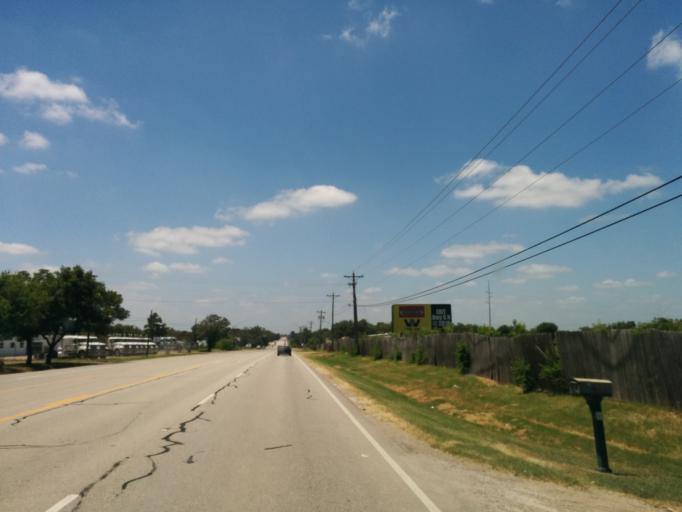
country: US
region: Texas
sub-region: Brazos County
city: Bryan
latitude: 30.7150
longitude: -96.3424
